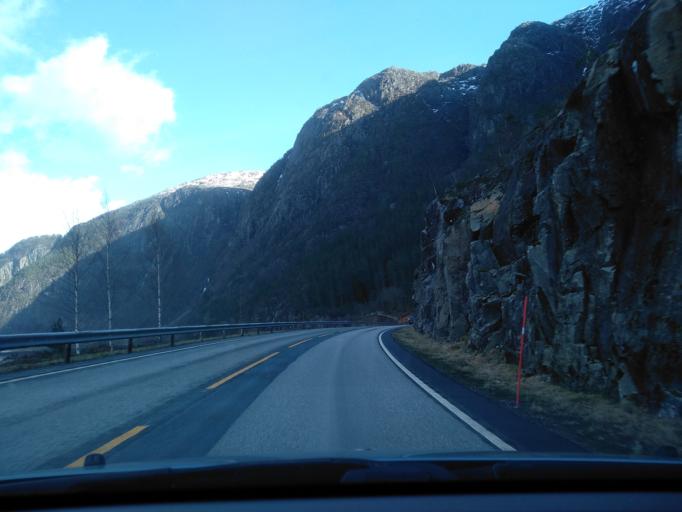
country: NO
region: Rogaland
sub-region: Sauda
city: Sauda
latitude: 59.8459
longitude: 6.3361
